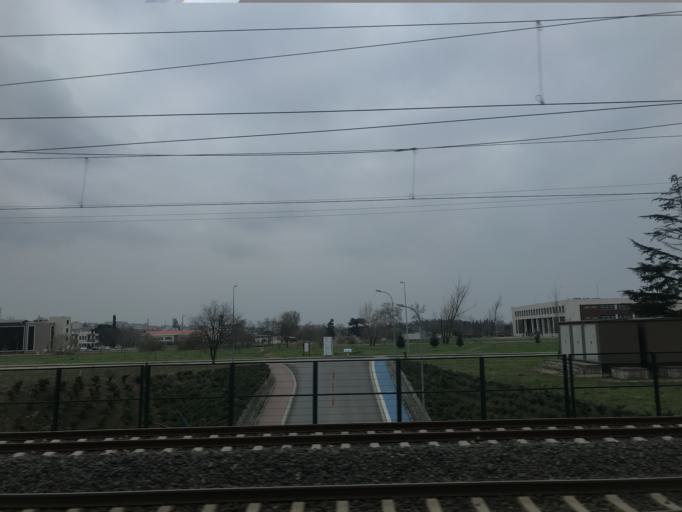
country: TR
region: Kocaeli
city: Darica
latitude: 40.8086
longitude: 29.3582
